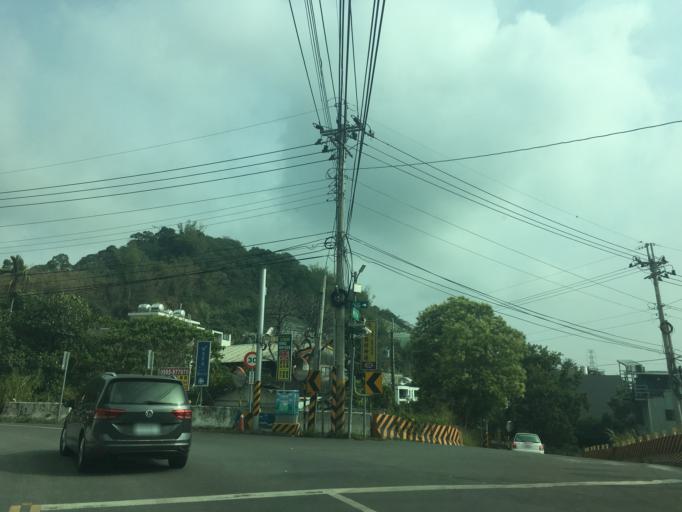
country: TW
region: Taiwan
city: Fengyuan
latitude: 24.2372
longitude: 120.7344
